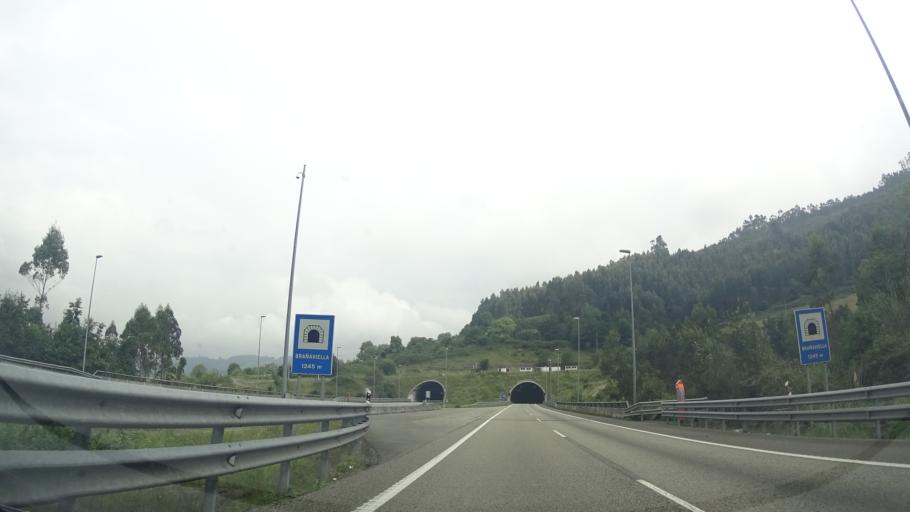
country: ES
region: Asturias
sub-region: Province of Asturias
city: Arriba
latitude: 43.4805
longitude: -5.5273
